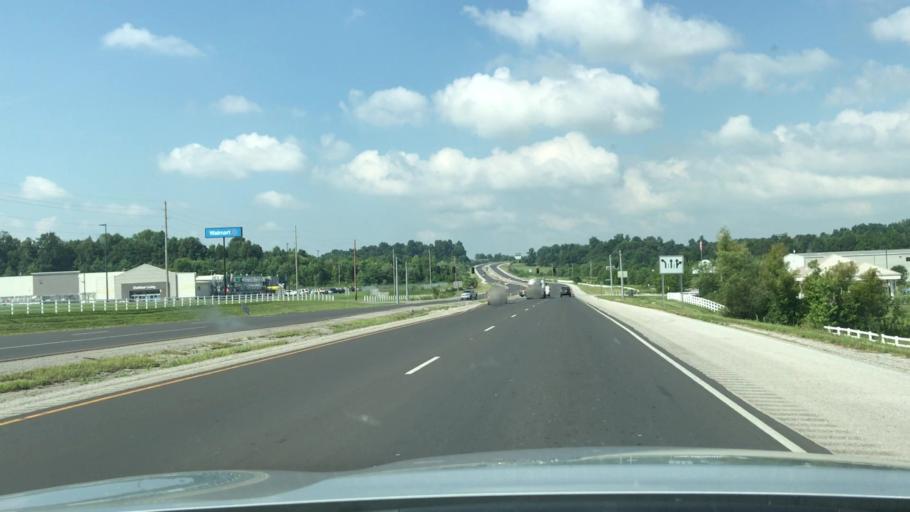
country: US
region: Kentucky
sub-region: Barren County
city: Glasgow
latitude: 37.0238
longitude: -85.9370
